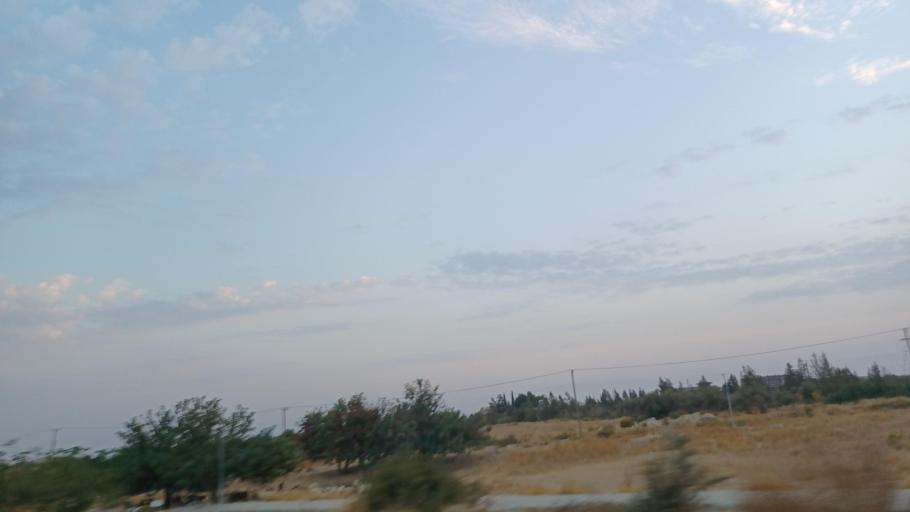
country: CY
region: Limassol
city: Ypsonas
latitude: 34.6993
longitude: 32.9733
